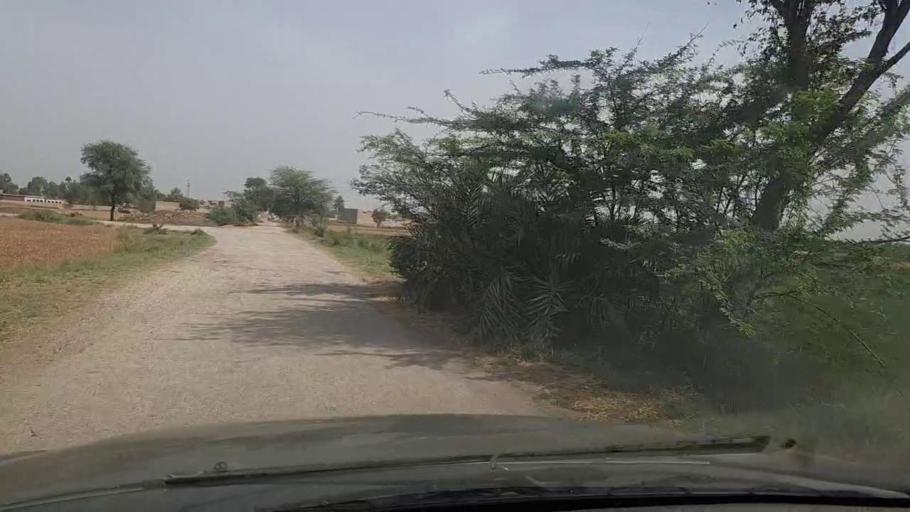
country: PK
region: Sindh
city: Chak
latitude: 27.8329
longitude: 68.7723
